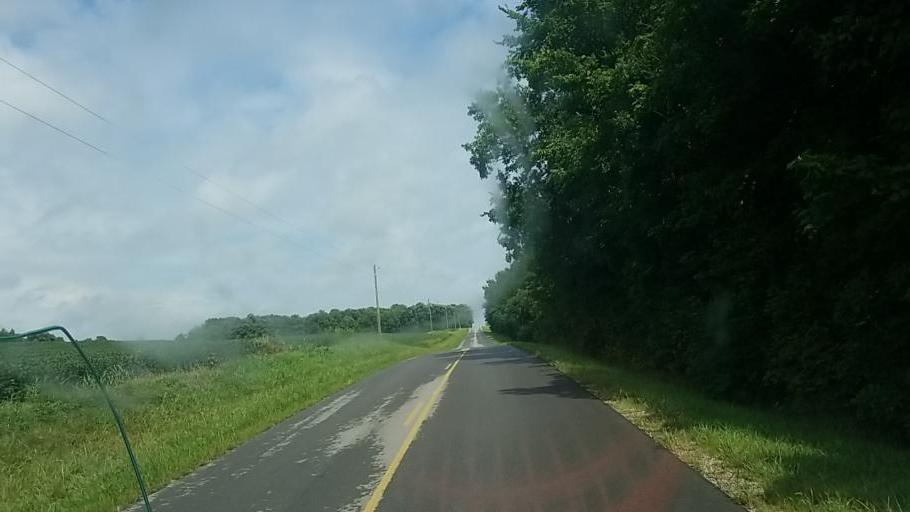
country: US
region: Ohio
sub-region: Logan County
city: West Liberty
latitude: 40.2381
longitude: -83.6568
